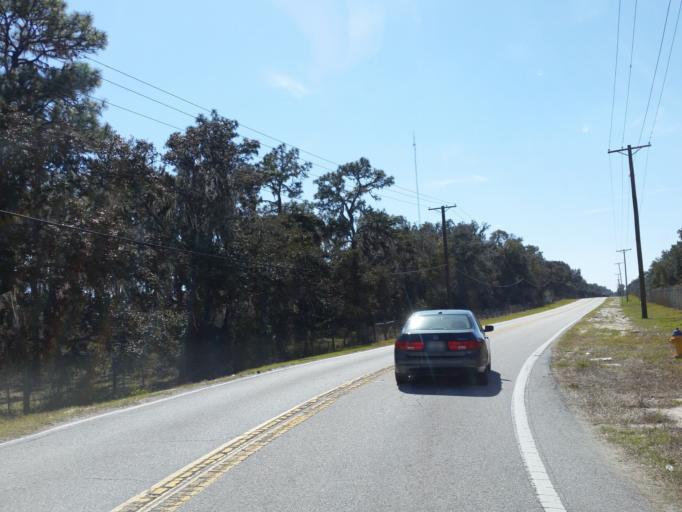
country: US
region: Florida
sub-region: Hillsborough County
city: Boyette
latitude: 27.8351
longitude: -82.2444
